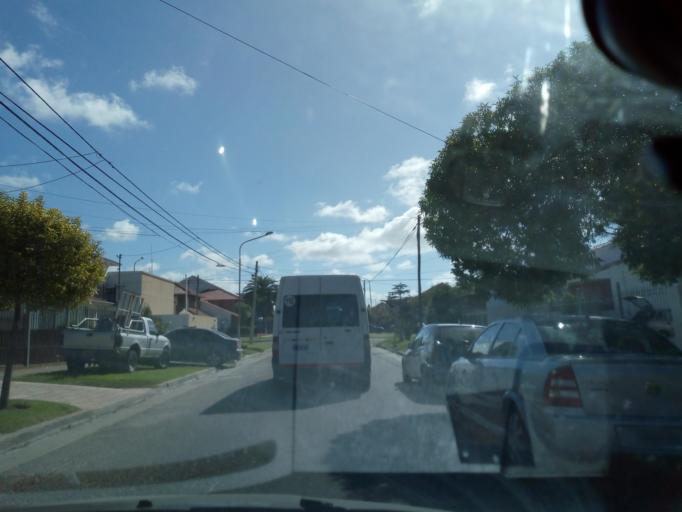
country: AR
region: Buenos Aires
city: Mar del Plata
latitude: -38.0520
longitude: -57.5567
